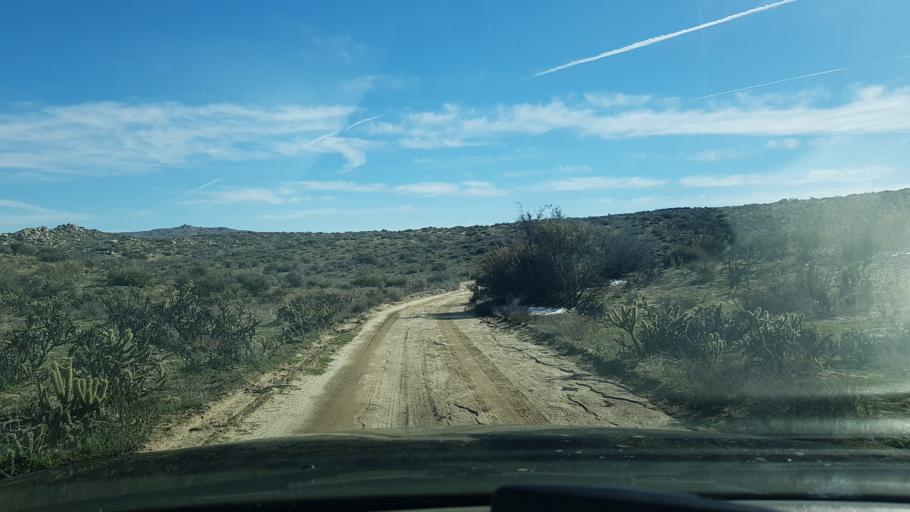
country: US
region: California
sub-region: San Diego County
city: Borrego Springs
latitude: 33.2055
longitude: -116.4878
